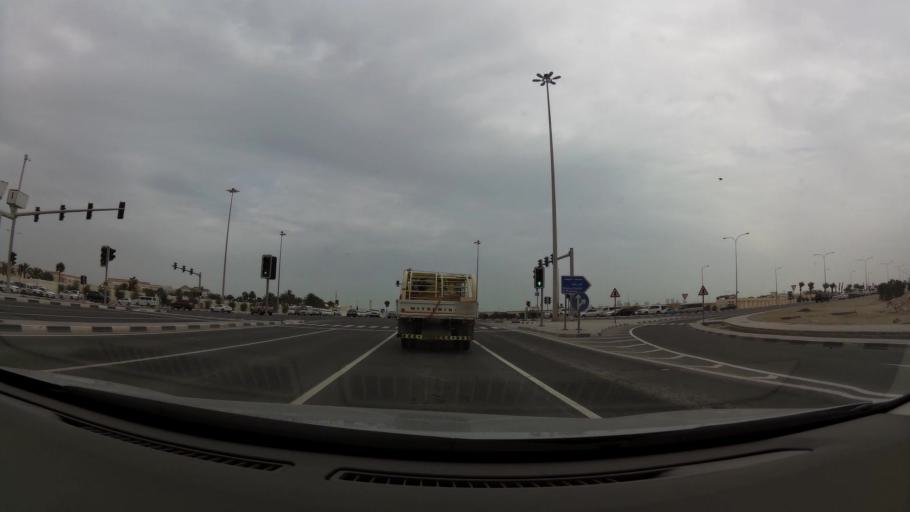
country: QA
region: Baladiyat ar Rayyan
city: Ar Rayyan
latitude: 25.3491
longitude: 51.4783
